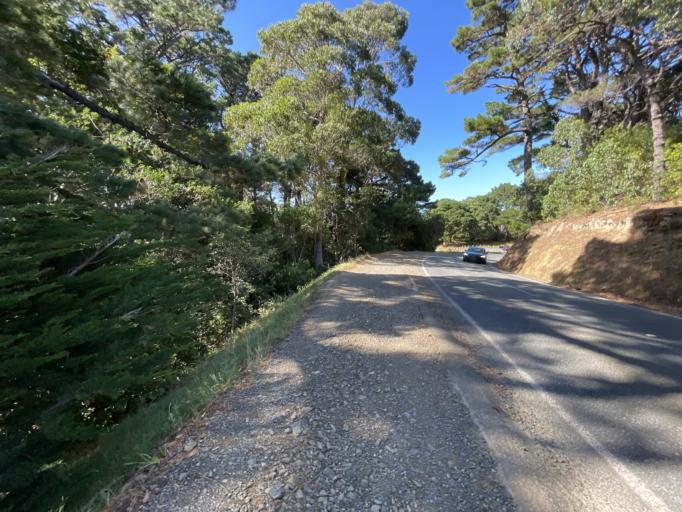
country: NZ
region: Wellington
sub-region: Wellington City
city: Wellington
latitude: -41.3089
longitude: 174.7882
